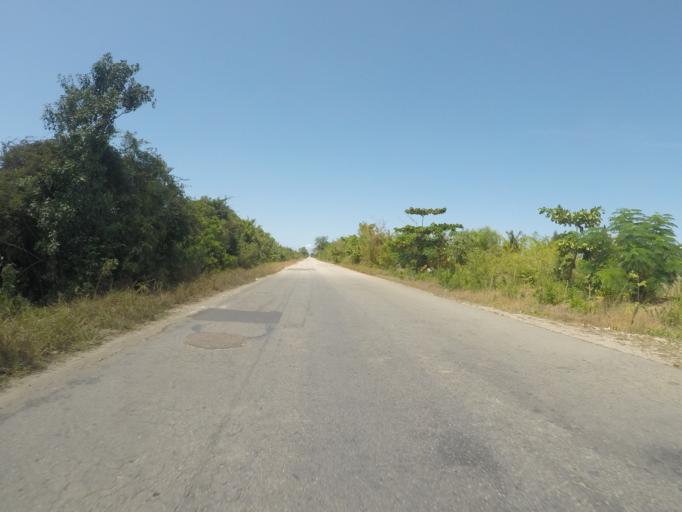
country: TZ
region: Zanzibar Central/South
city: Nganane
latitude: -6.2712
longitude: 39.5030
